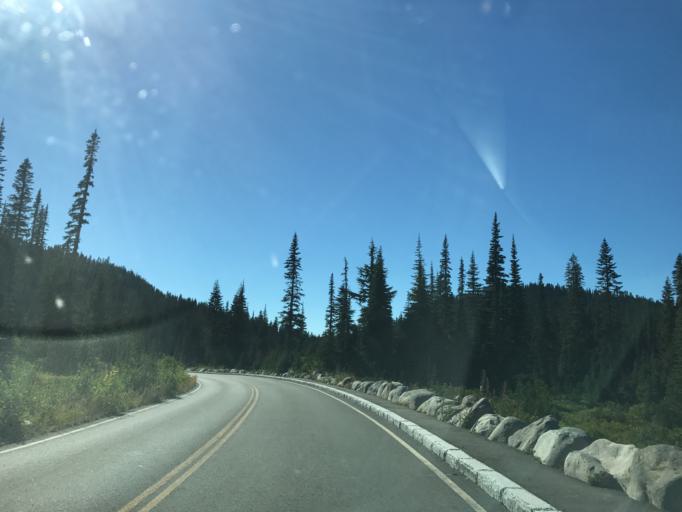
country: US
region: Washington
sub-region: Pierce County
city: Buckley
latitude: 46.7691
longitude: -121.7250
